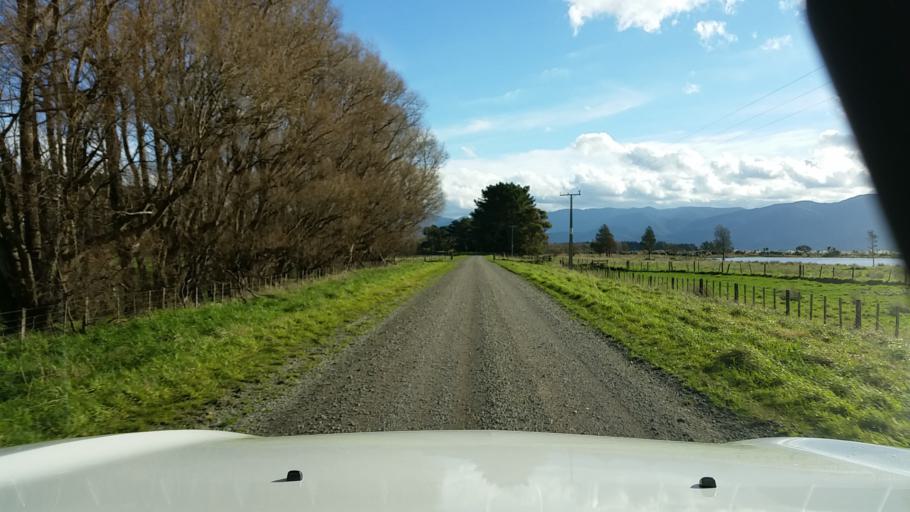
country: NZ
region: Wellington
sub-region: Upper Hutt City
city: Upper Hutt
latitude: -41.2504
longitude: 175.2485
